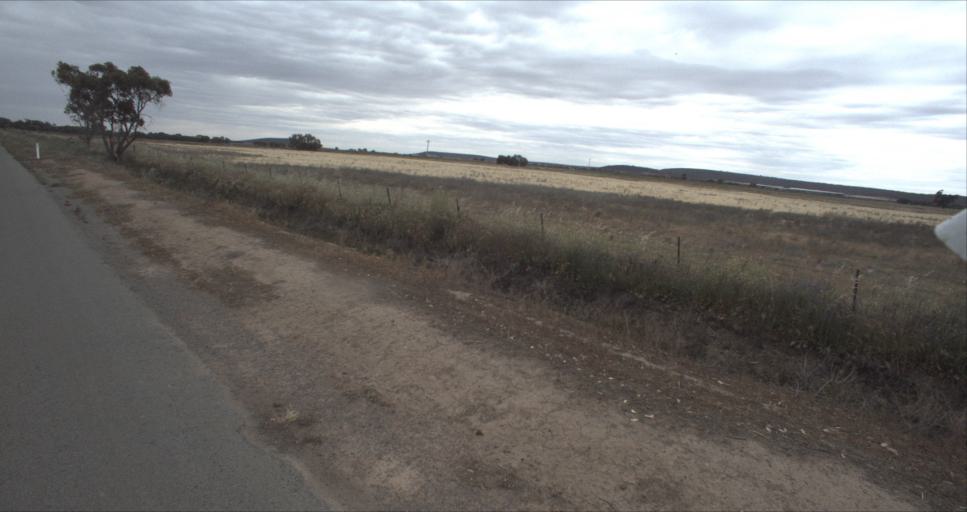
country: AU
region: New South Wales
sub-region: Leeton
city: Leeton
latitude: -34.4196
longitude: 146.3388
